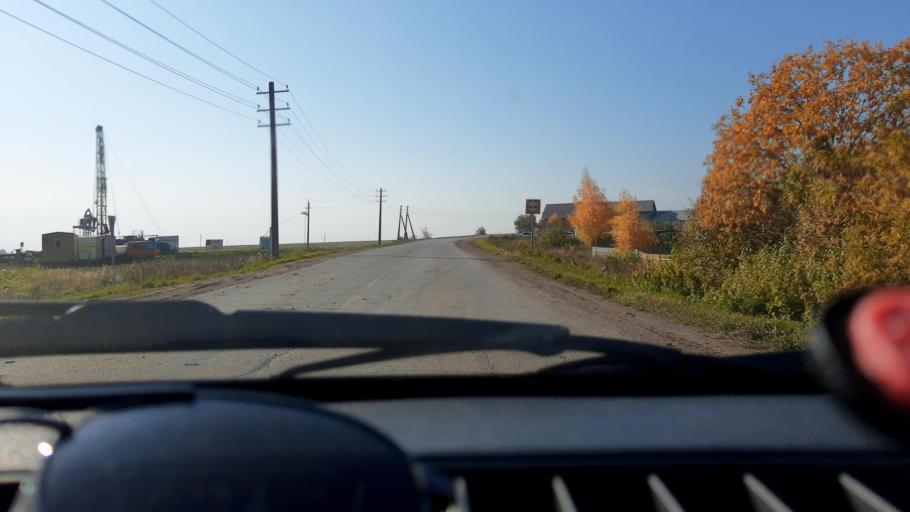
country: RU
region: Bashkortostan
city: Mikhaylovka
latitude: 54.8430
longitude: 55.8414
